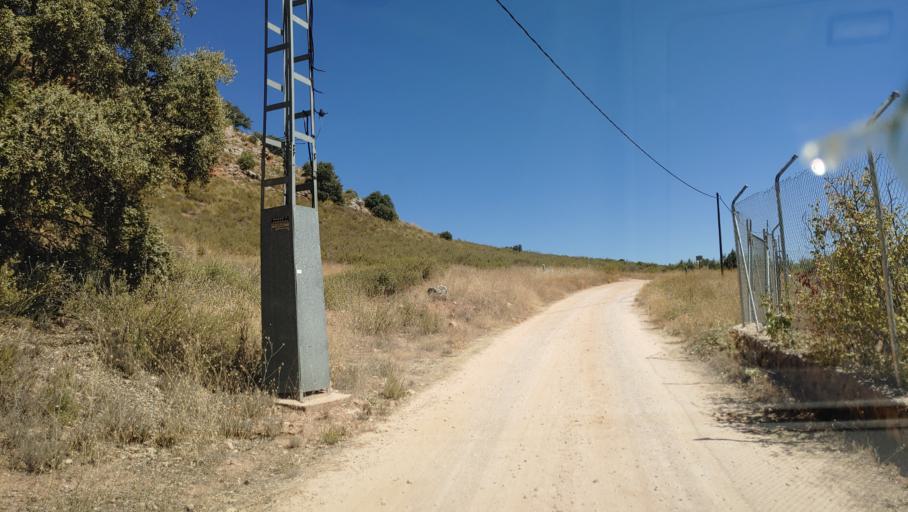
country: ES
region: Castille-La Mancha
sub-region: Provincia de Ciudad Real
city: Ruidera
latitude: 38.9273
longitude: -2.8197
